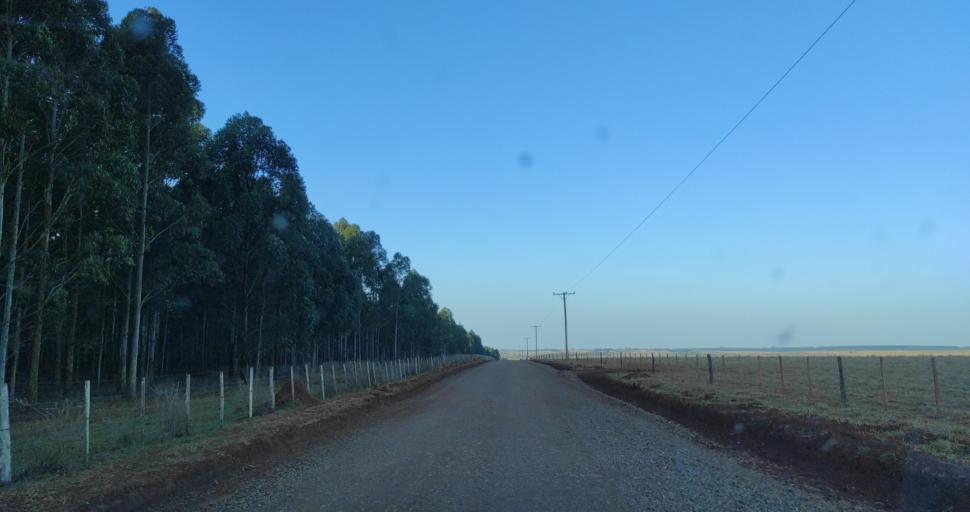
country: PY
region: Itapua
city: San Juan del Parana
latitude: -27.4242
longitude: -56.0901
